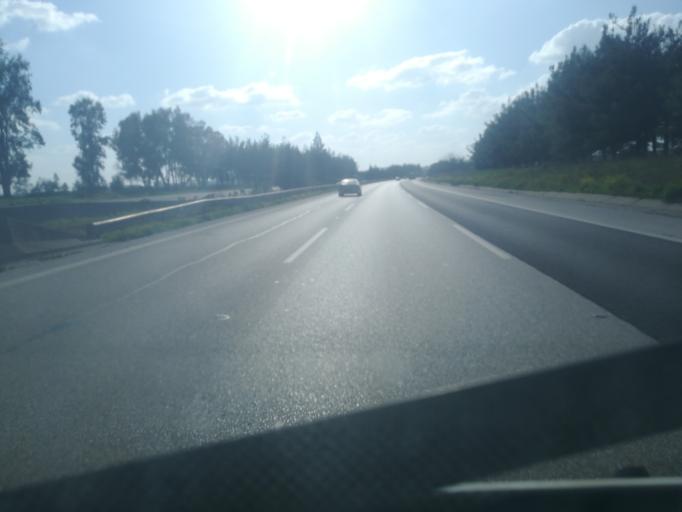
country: TR
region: Adana
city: Yakapinar
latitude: 37.0048
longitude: 35.6669
